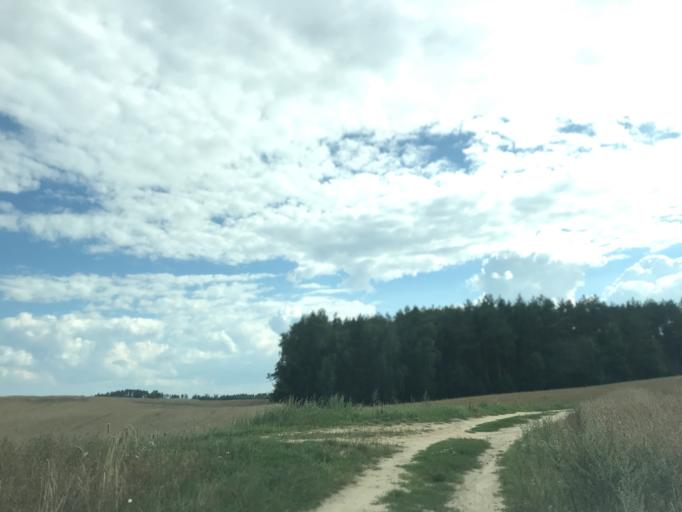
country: PL
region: Kujawsko-Pomorskie
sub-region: Powiat brodnicki
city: Brzozie
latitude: 53.3155
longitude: 19.6872
